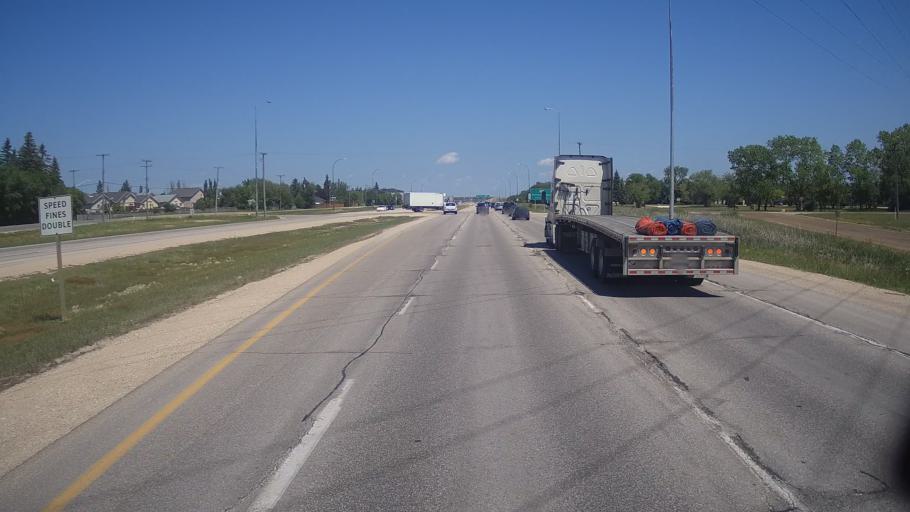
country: CA
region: Manitoba
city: Winnipeg
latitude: 49.9365
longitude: -97.0396
